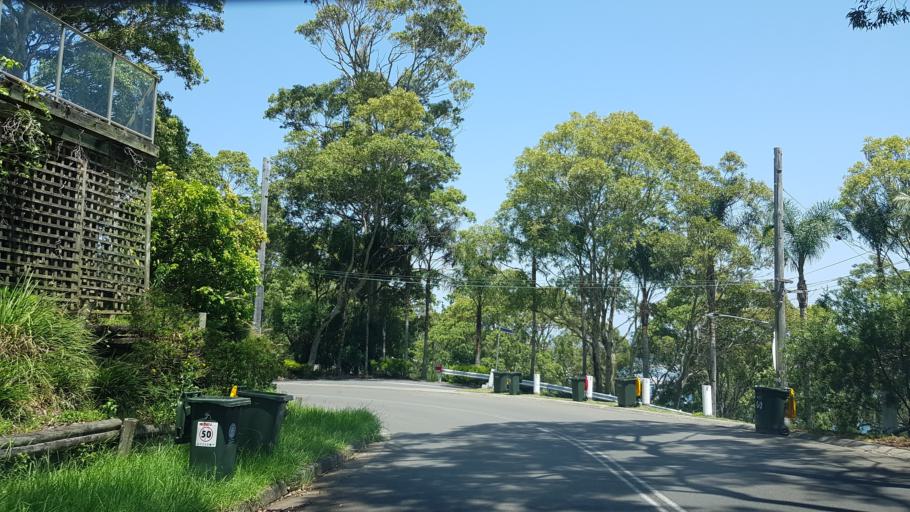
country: AU
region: New South Wales
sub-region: Pittwater
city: Bay View
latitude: -33.6506
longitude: 151.3034
